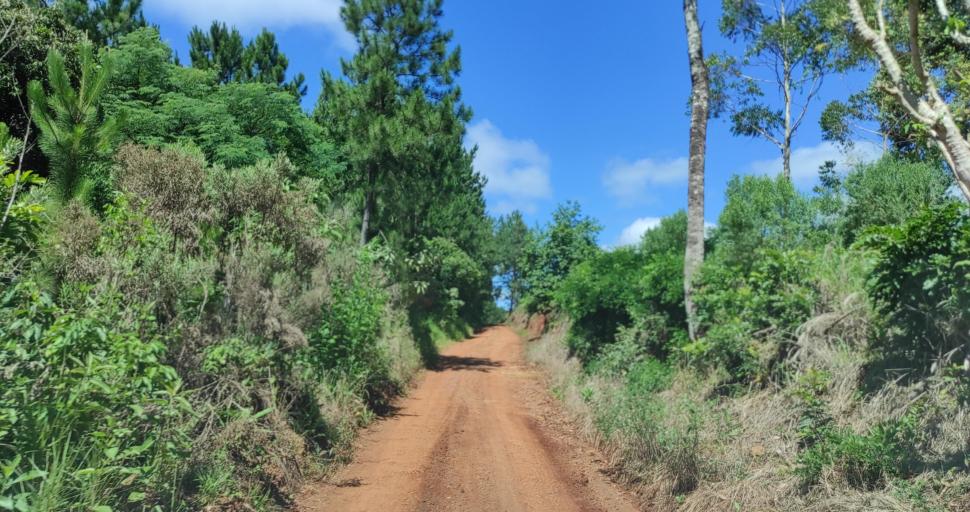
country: AR
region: Misiones
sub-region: Departamento de Veinticinco de Mayo
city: Veinticinco de Mayo
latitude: -27.4183
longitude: -54.7318
